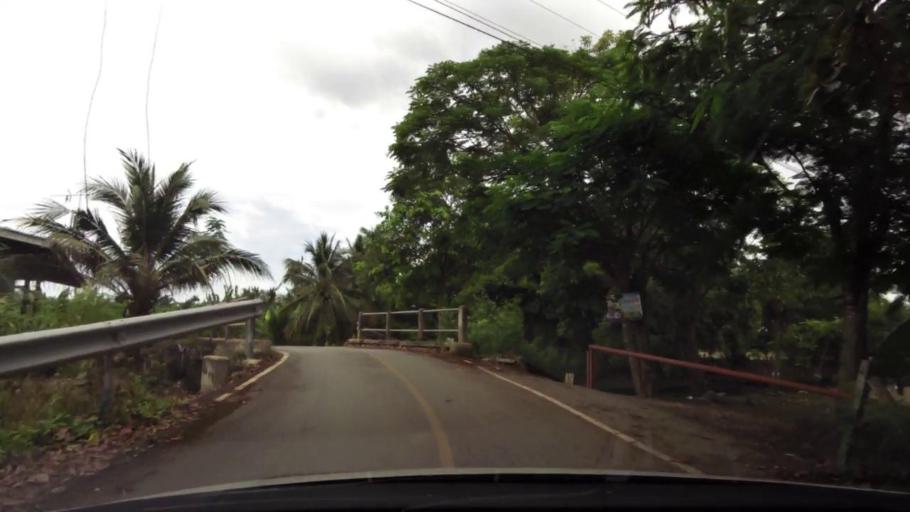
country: TH
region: Samut Sakhon
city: Ban Phaeo
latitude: 13.5618
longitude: 100.0338
